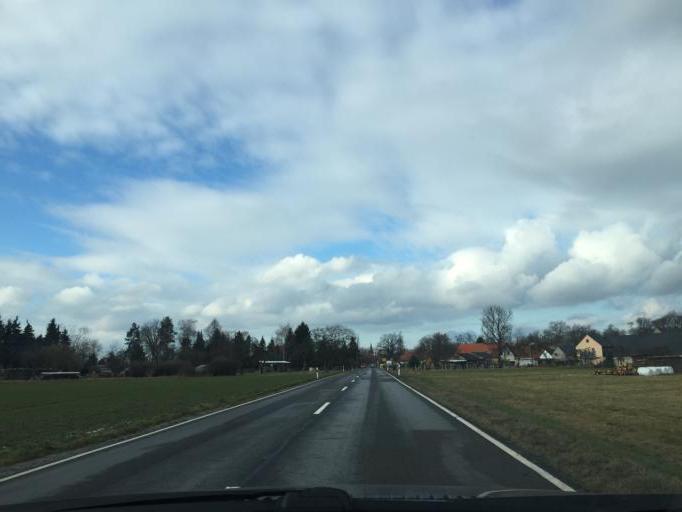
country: DE
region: Saxony
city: Wachau
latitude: 51.1555
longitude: 13.8883
